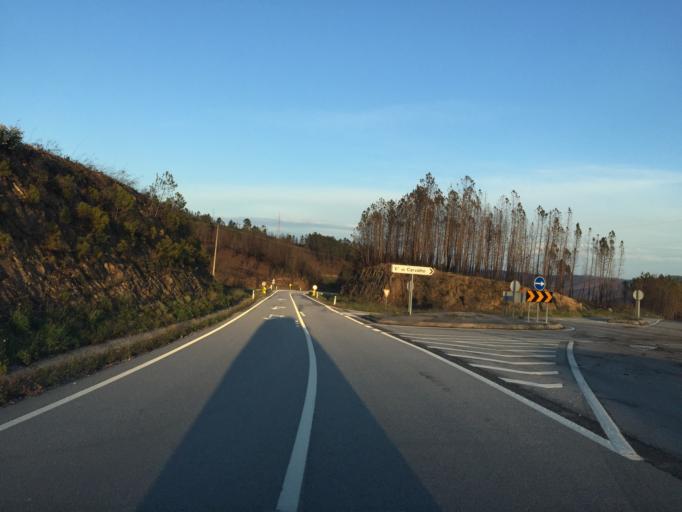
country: PT
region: Coimbra
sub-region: Pampilhosa da Serra
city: Pampilhosa da Serra
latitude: 40.0798
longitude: -7.9832
